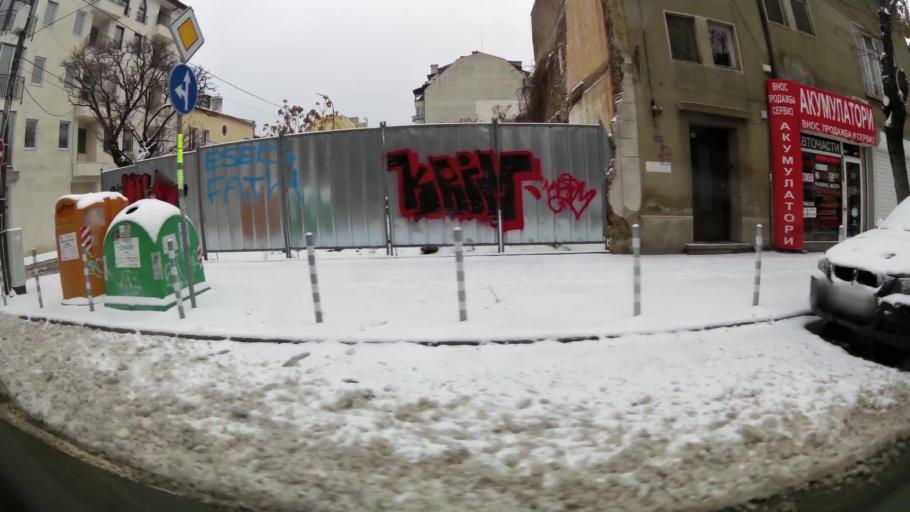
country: BG
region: Sofia-Capital
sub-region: Stolichna Obshtina
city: Sofia
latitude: 42.7037
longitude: 23.3072
